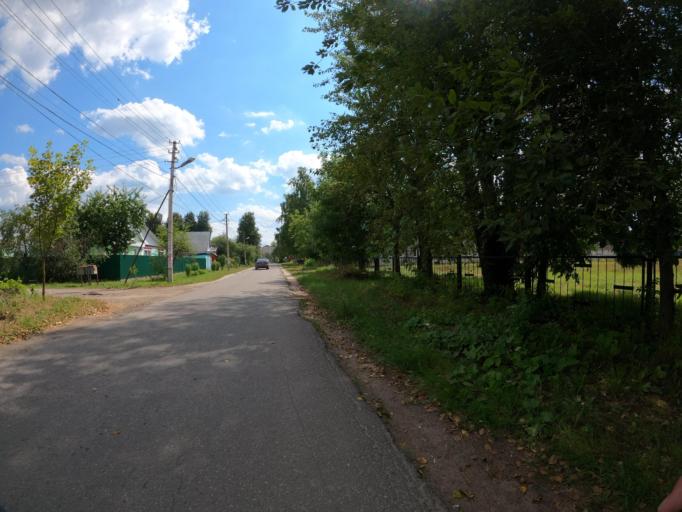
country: RU
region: Moskovskaya
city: Lopatinskiy
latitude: 55.2797
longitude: 38.7444
